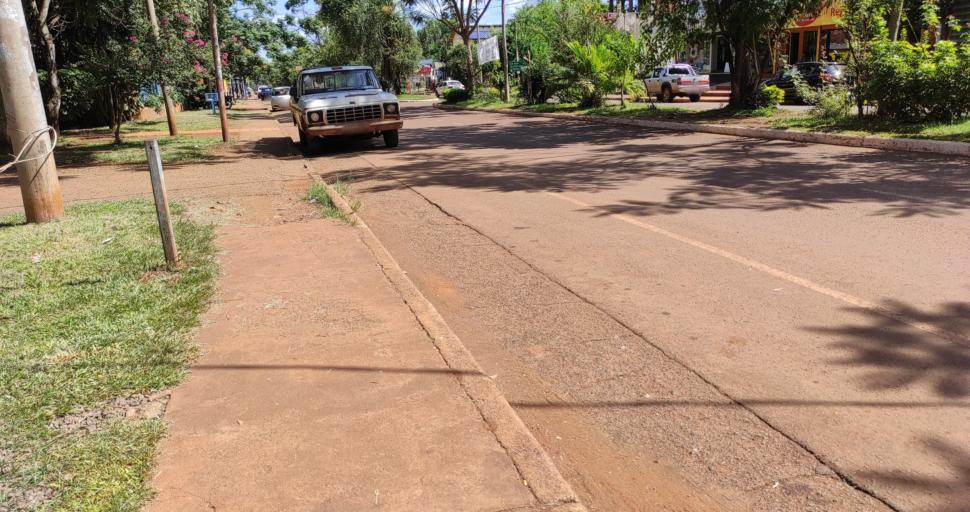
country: AR
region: Misiones
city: El Soberbio
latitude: -27.2953
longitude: -54.1981
